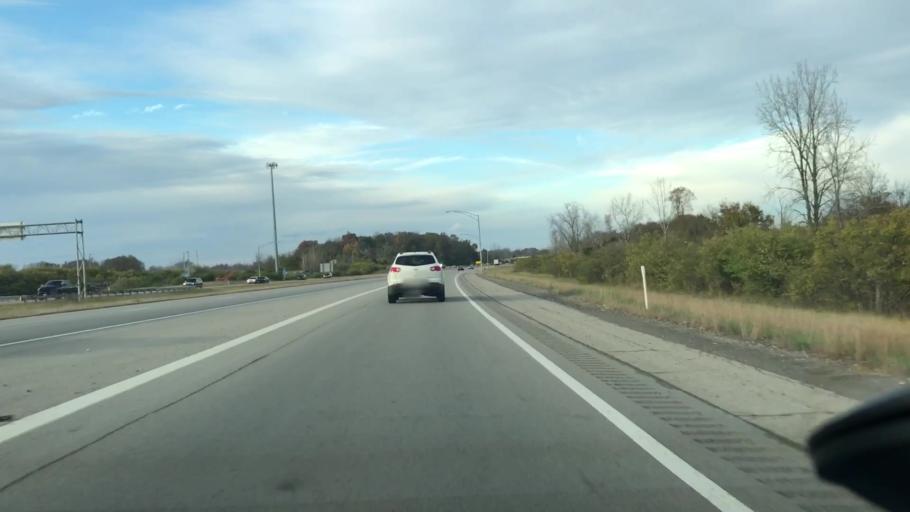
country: US
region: Ohio
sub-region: Clark County
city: Holiday Valley
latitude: 39.8475
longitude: -83.9935
